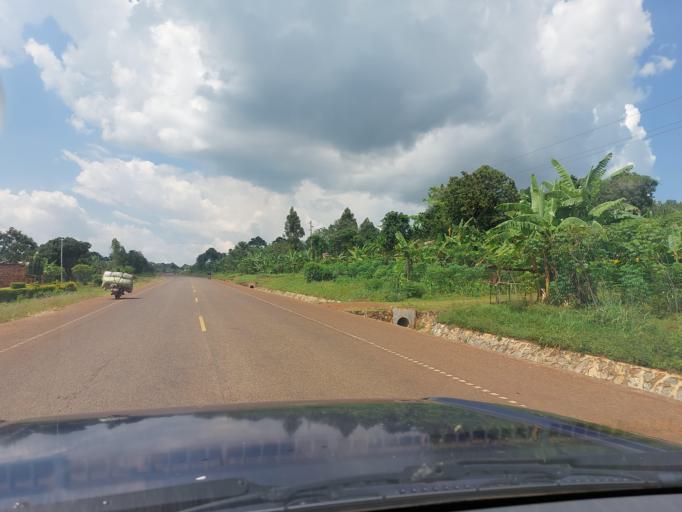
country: UG
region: Central Region
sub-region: Buikwe District
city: Buikwe
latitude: 0.3235
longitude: 33.1142
